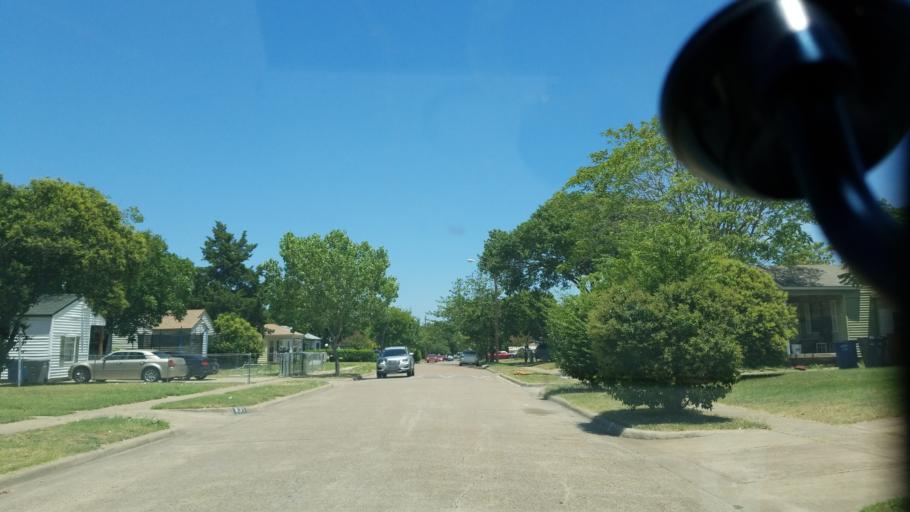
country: US
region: Texas
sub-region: Dallas County
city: Cockrell Hill
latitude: 32.7098
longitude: -96.8336
